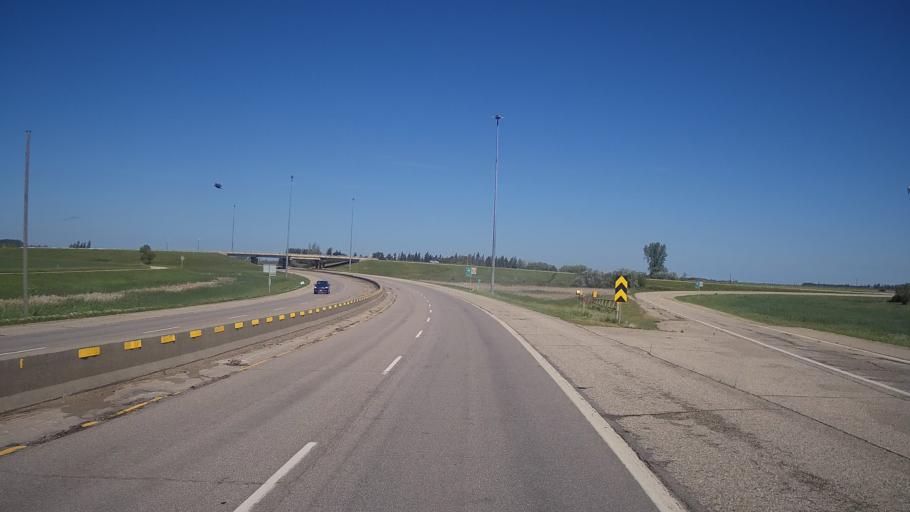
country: CA
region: Manitoba
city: Portage la Prairie
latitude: 49.9710
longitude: -98.3592
